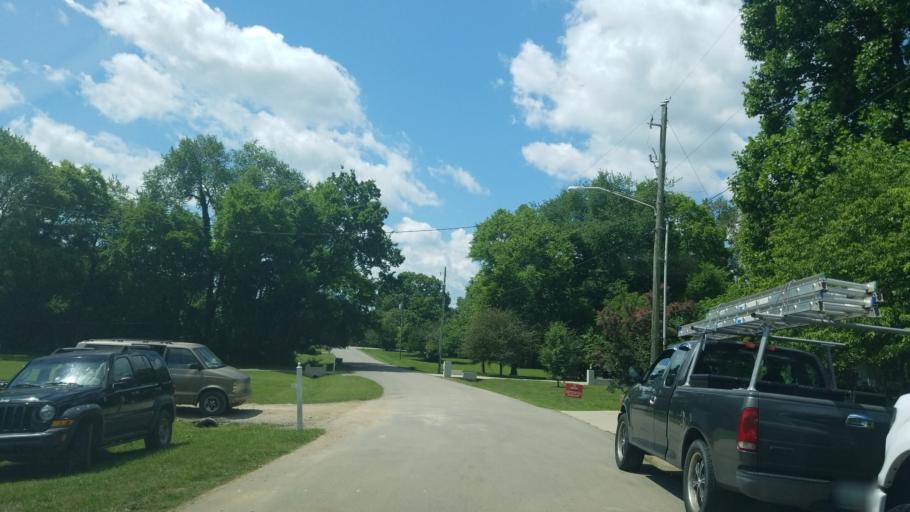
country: US
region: Tennessee
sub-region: Williamson County
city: Brentwood
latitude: 36.0271
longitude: -86.8003
